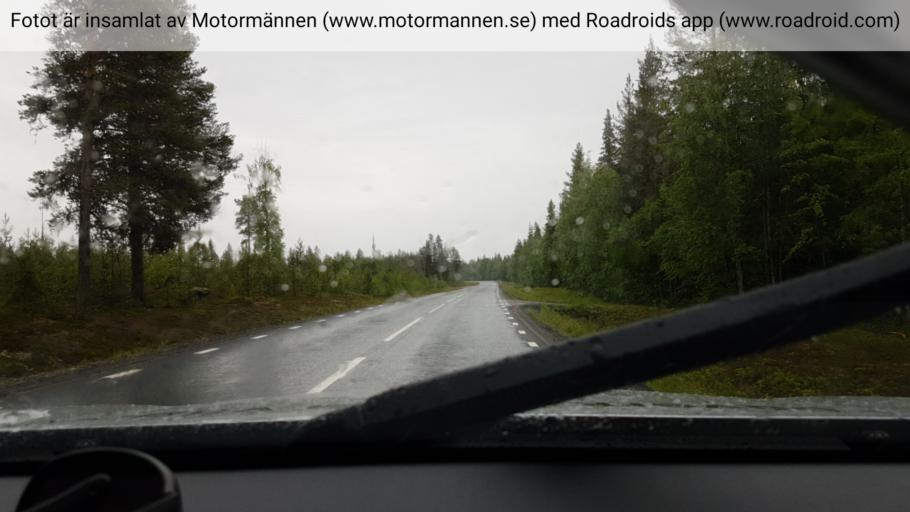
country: SE
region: Vaesterbotten
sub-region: Lycksele Kommun
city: Soderfors
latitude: 65.2736
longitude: 17.9579
